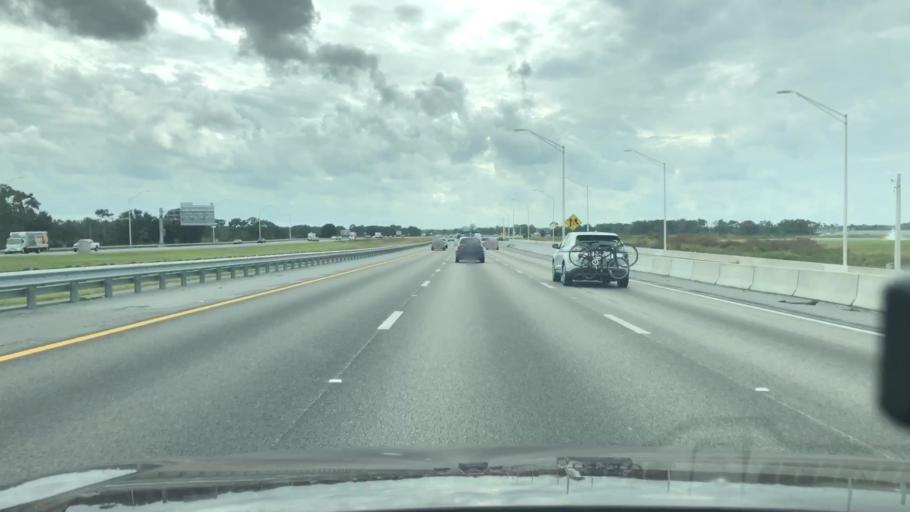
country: US
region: Florida
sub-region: Sarasota County
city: The Meadows
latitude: 27.3852
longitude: -82.4482
